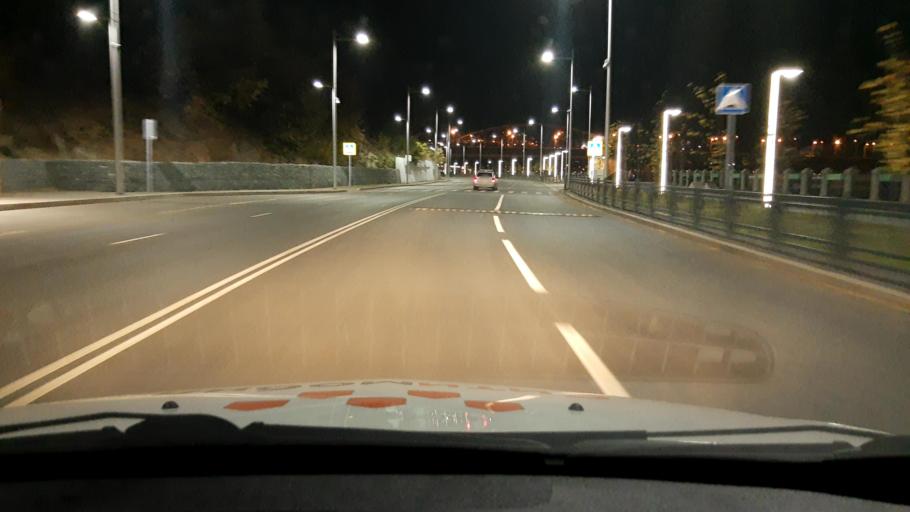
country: RU
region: Bashkortostan
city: Ufa
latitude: 54.7124
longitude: 55.9486
